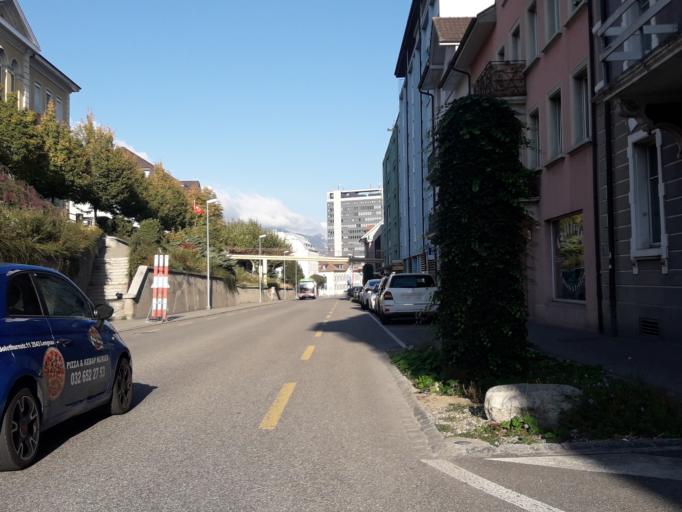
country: CH
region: Solothurn
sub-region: Bezirk Lebern
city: Grenchen
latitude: 47.1910
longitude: 7.3926
